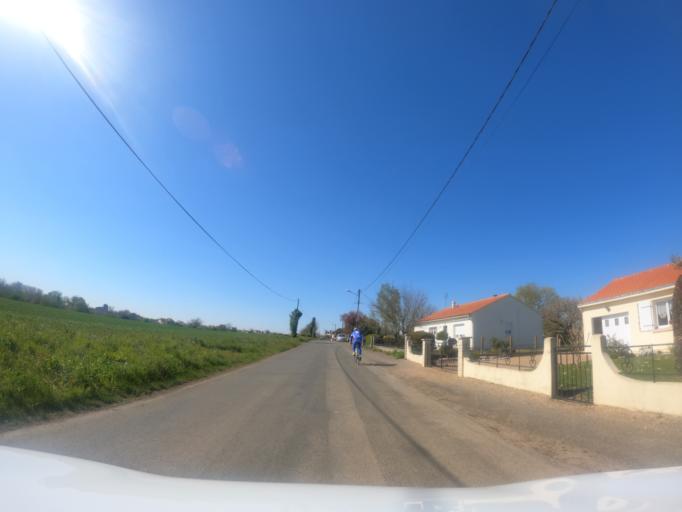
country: FR
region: Pays de la Loire
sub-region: Departement de la Vendee
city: Fontenay-le-Comte
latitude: 46.4221
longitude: -0.8126
